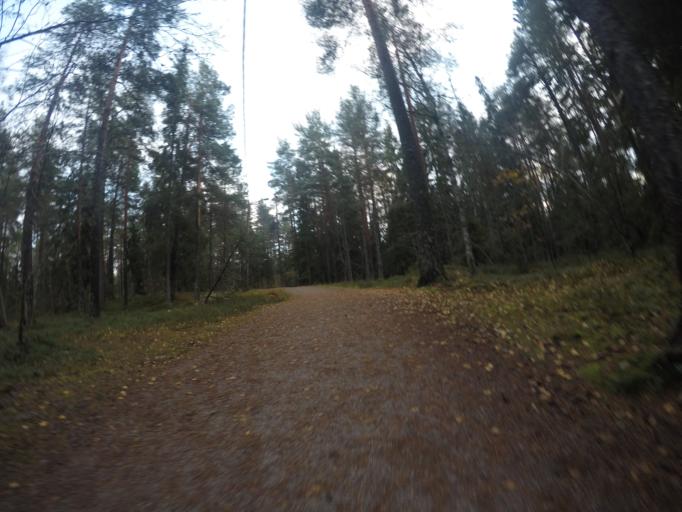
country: SE
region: Soedermanland
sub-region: Eskilstuna Kommun
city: Eskilstuna
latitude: 59.3470
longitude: 16.5254
